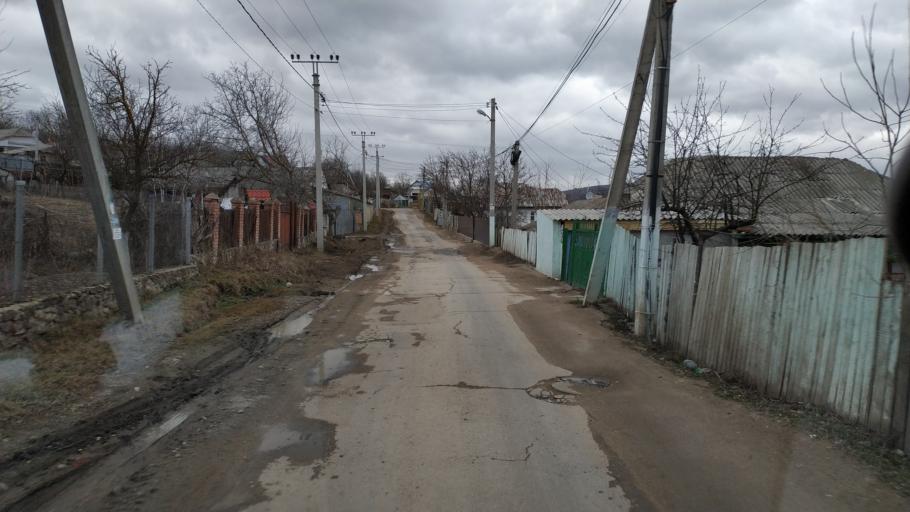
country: MD
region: Calarasi
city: Calarasi
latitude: 47.2426
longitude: 28.3068
